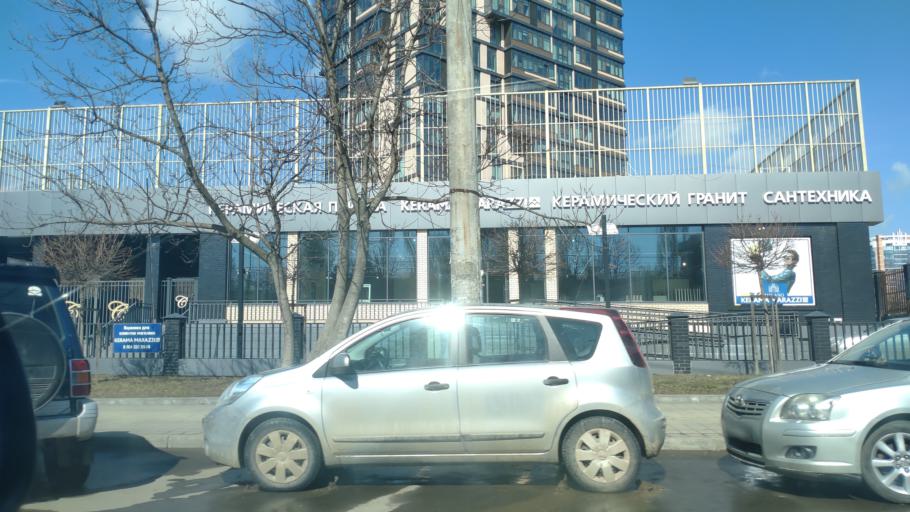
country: RU
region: Krasnodarskiy
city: Krasnodar
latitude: 45.0549
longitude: 38.9985
